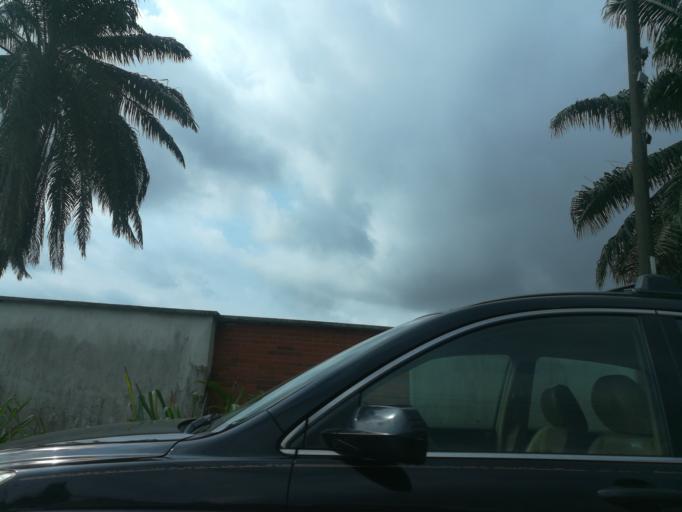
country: NG
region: Lagos
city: Ojota
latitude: 6.5780
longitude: 3.3575
